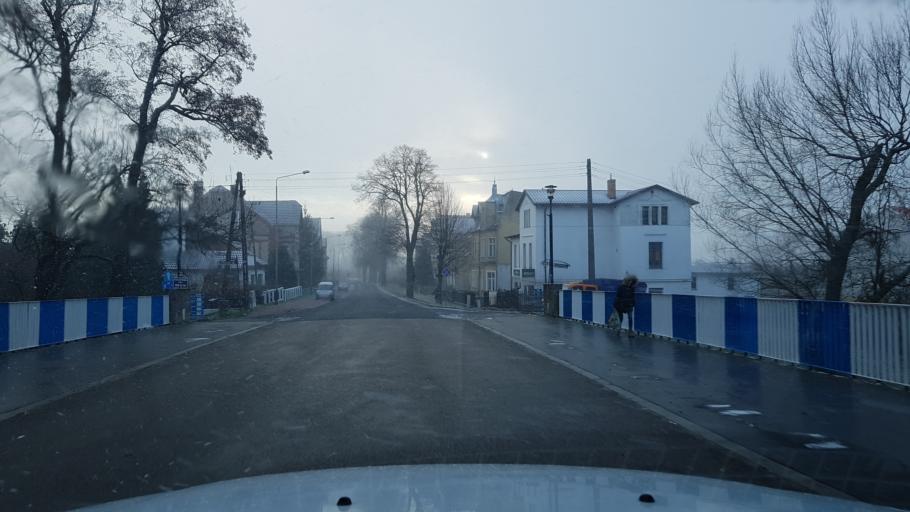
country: PL
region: West Pomeranian Voivodeship
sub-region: Powiat gryficki
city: Trzebiatow
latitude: 54.0627
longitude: 15.2699
